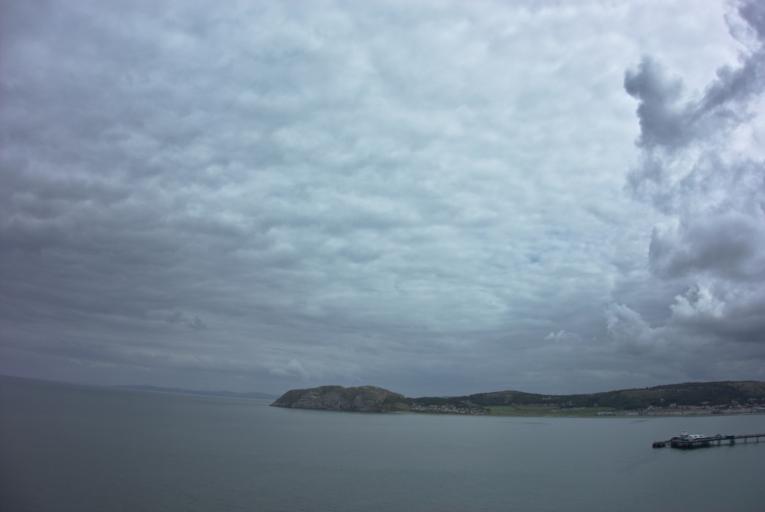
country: GB
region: Wales
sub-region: Conwy
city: Llandudno
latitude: 53.3368
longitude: -3.8320
